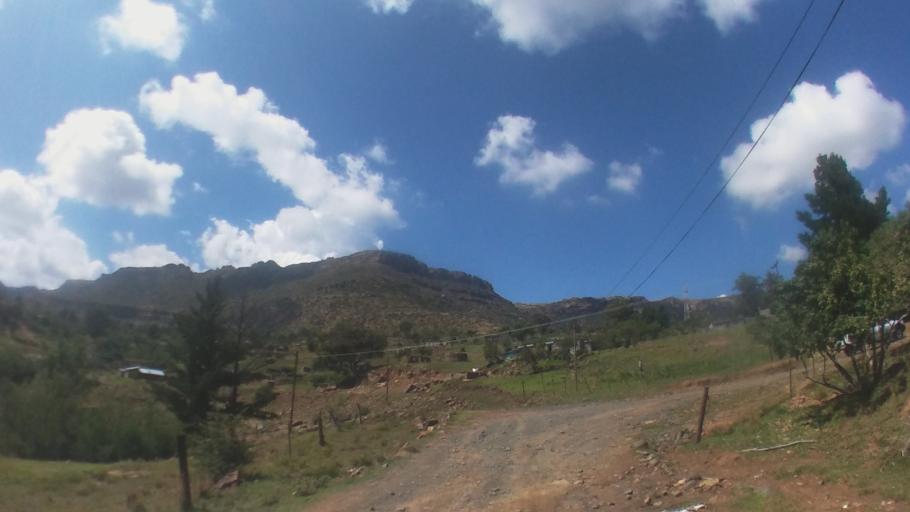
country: LS
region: Maseru
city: Nako
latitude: -29.6239
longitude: 27.5155
